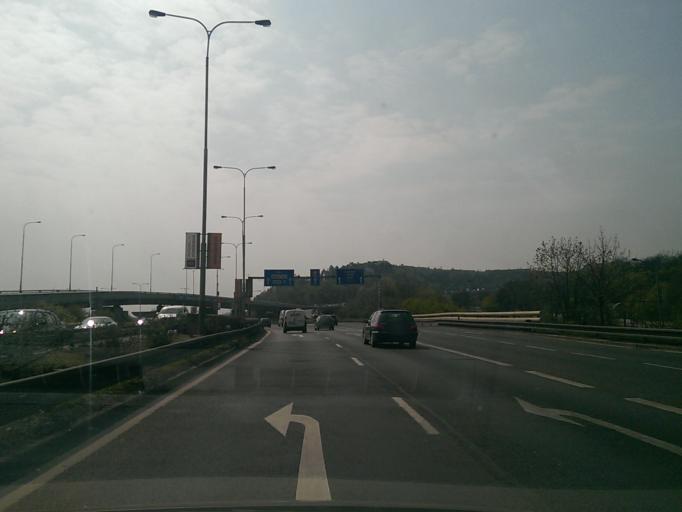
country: CZ
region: Praha
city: Branik
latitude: 50.0427
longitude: 14.4070
